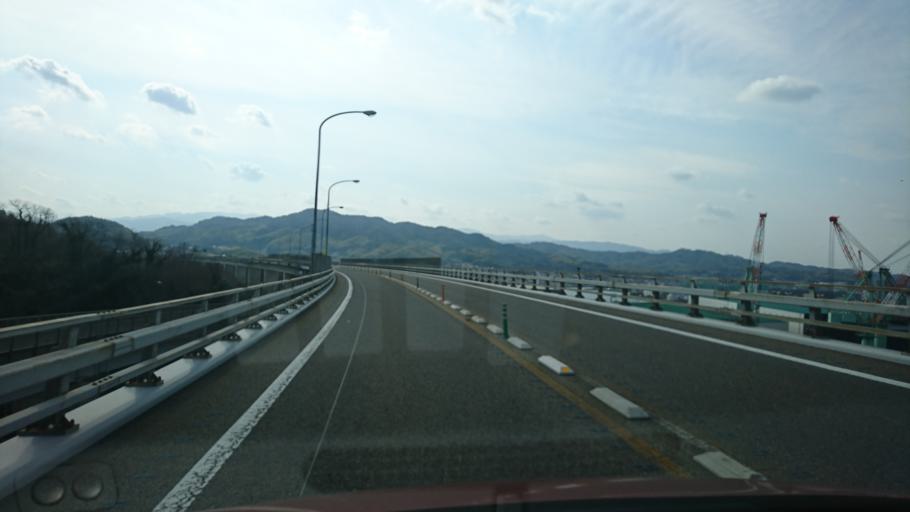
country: JP
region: Hiroshima
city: Takehara
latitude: 34.1105
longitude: 132.9766
